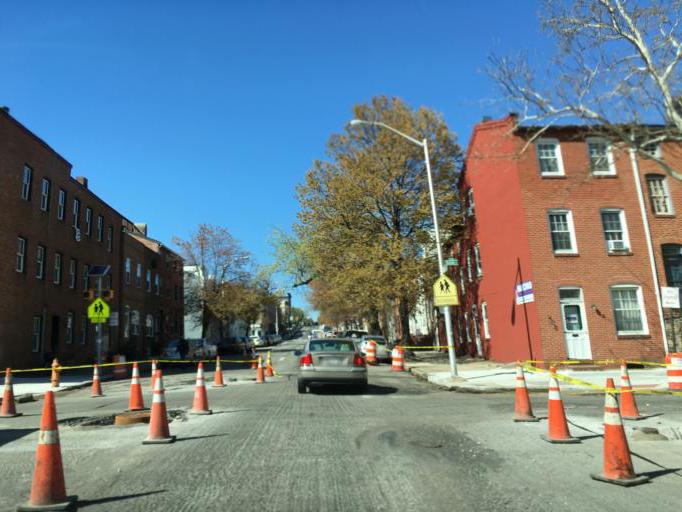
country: US
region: Maryland
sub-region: City of Baltimore
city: Baltimore
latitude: 39.2867
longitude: -76.5888
